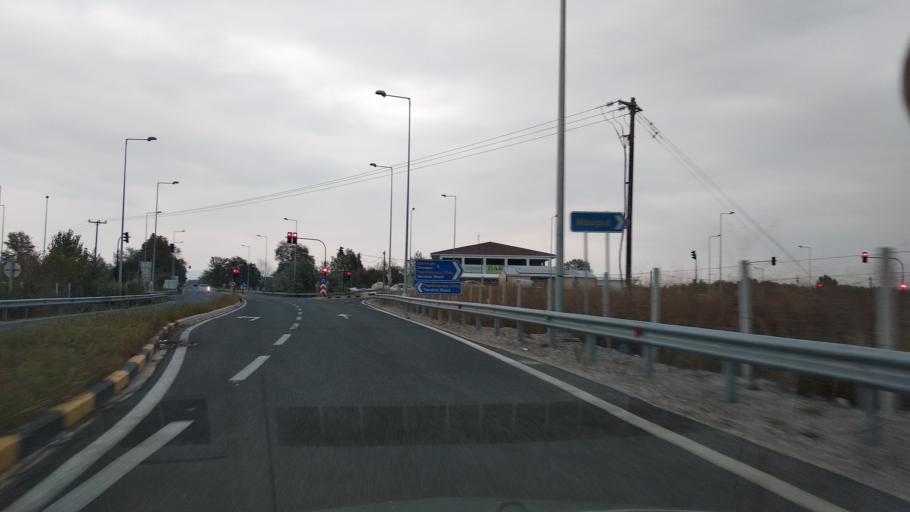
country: GR
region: Thessaly
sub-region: Trikala
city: Pigi
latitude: 39.5245
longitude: 21.7298
